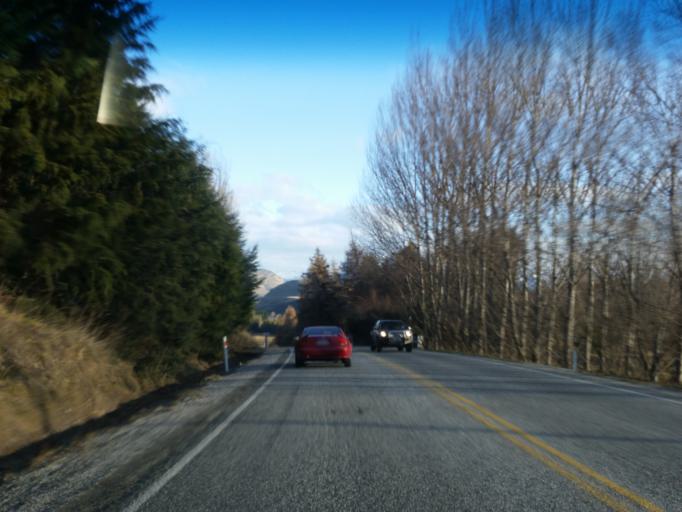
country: NZ
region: Otago
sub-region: Queenstown-Lakes District
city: Arrowtown
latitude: -44.9523
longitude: 168.8199
